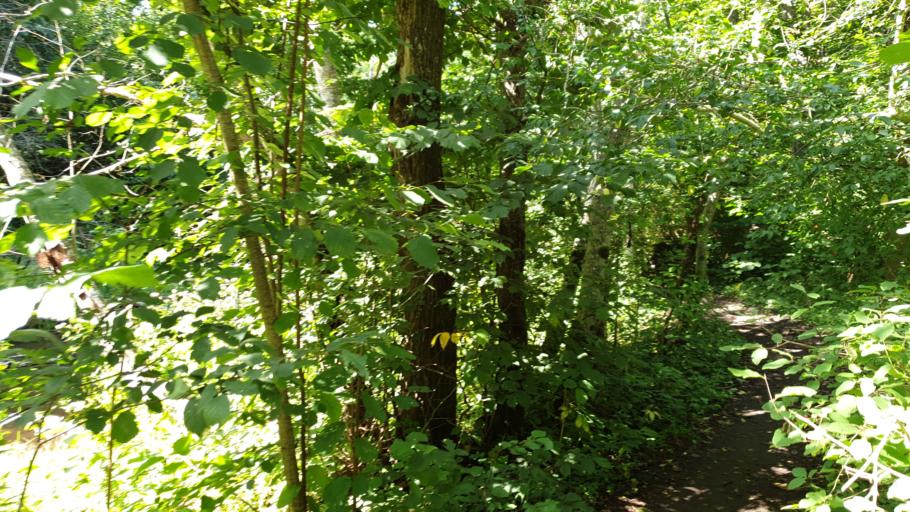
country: LT
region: Vilnius County
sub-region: Vilniaus Rajonas
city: Vievis
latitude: 54.8208
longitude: 24.9358
